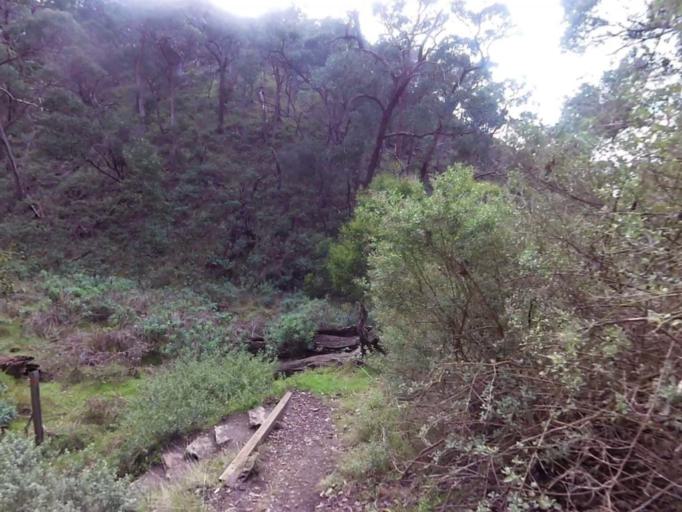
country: AU
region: Victoria
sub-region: Moorabool
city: Bacchus Marsh
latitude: -37.6631
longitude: 144.3346
